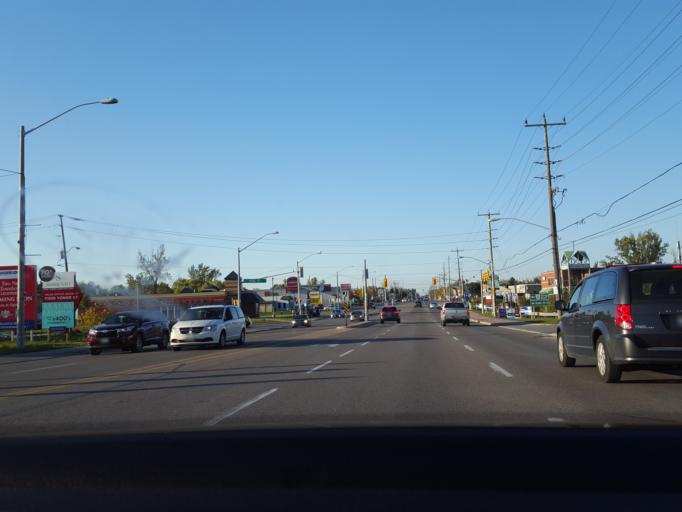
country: CA
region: Ontario
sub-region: York
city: Richmond Hill
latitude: 43.9436
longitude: -79.4544
